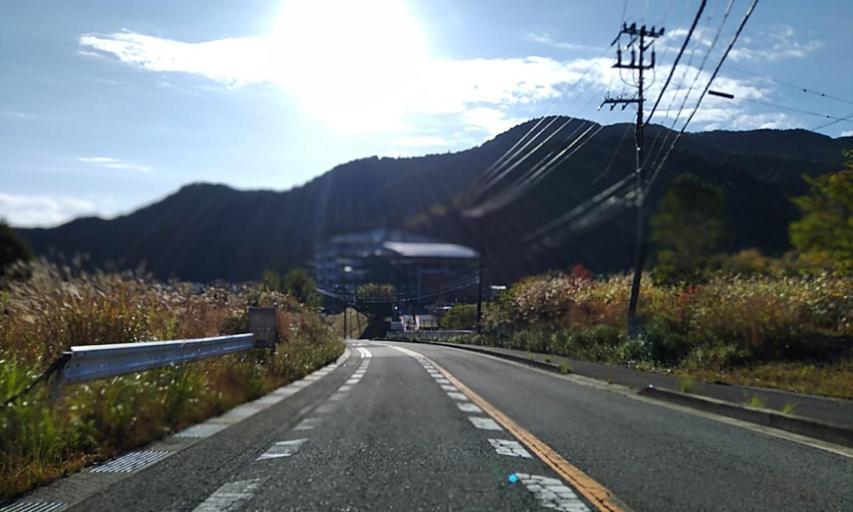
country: JP
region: Wakayama
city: Iwade
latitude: 34.1532
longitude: 135.3092
